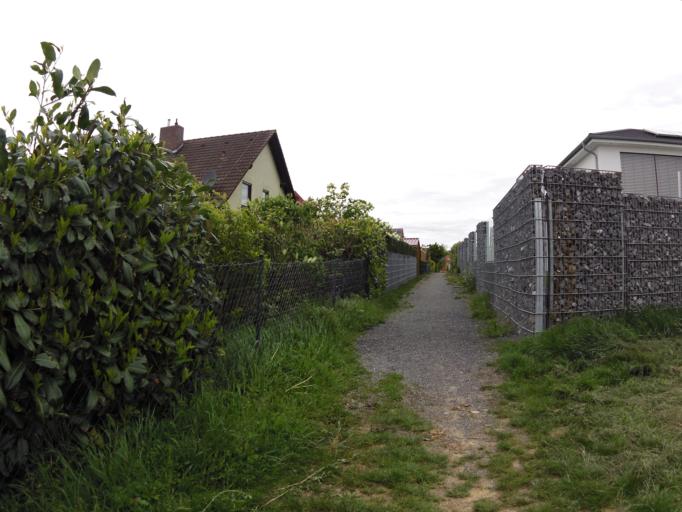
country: DE
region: Bavaria
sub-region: Regierungsbezirk Unterfranken
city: Kurnach
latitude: 49.8478
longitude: 10.0502
